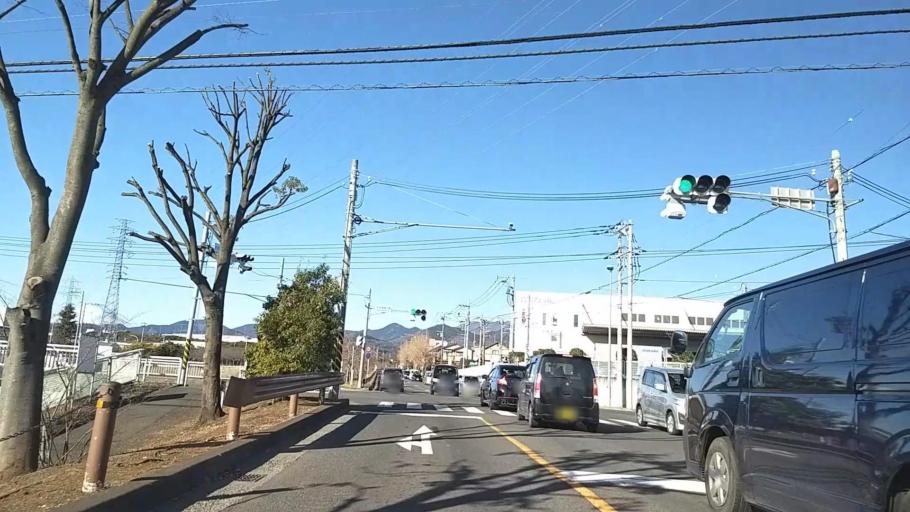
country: JP
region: Kanagawa
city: Hadano
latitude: 35.3834
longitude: 139.1993
